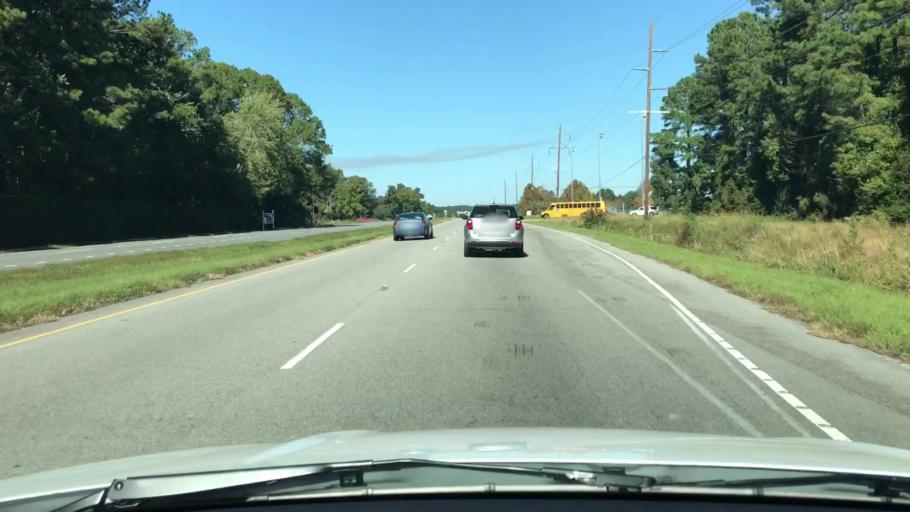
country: US
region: South Carolina
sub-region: Beaufort County
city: Laurel Bay
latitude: 32.5307
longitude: -80.7475
